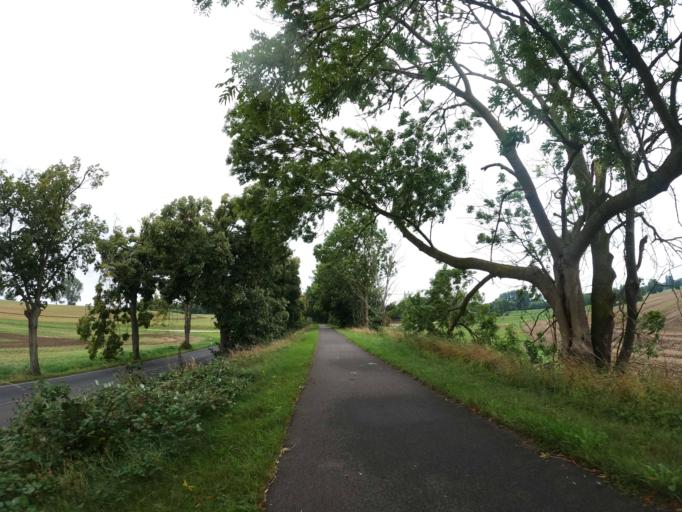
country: DE
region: Mecklenburg-Vorpommern
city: Poseritz
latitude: 54.2953
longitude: 13.2832
